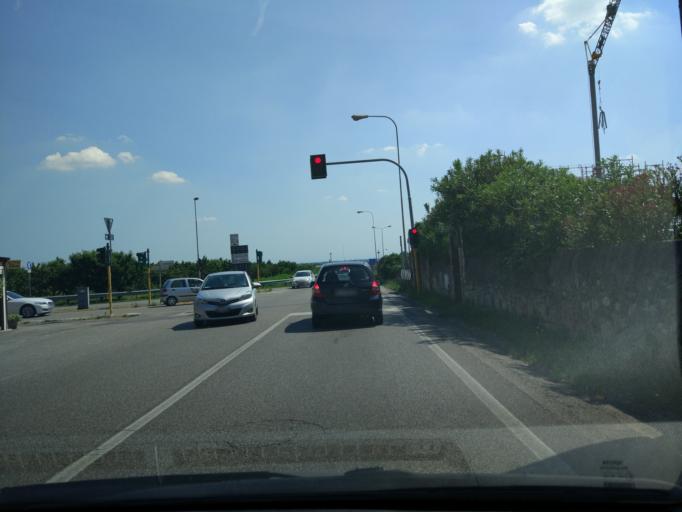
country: IT
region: Veneto
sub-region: Provincia di Verona
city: Colognola ai Colli
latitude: 45.4311
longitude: 11.1774
